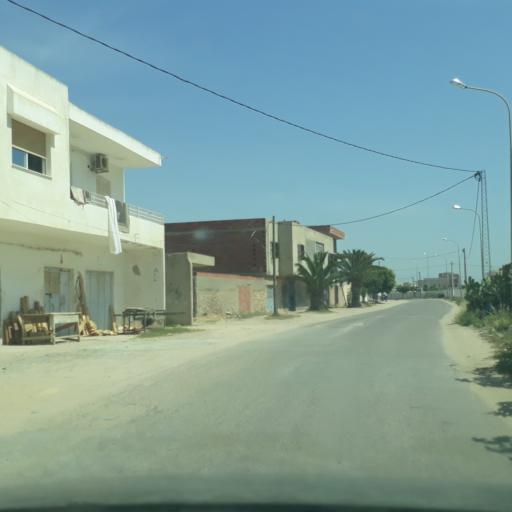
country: TN
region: Safaqis
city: Al Qarmadah
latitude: 34.8223
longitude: 10.7804
